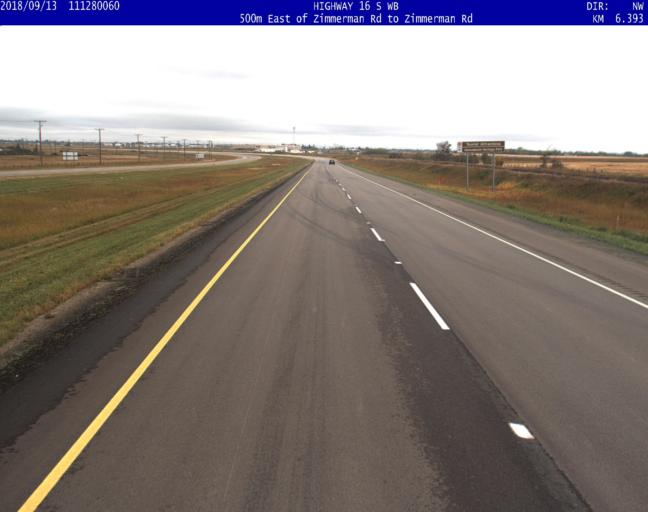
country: CA
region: Saskatchewan
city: Saskatoon
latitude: 52.0794
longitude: -106.5094
